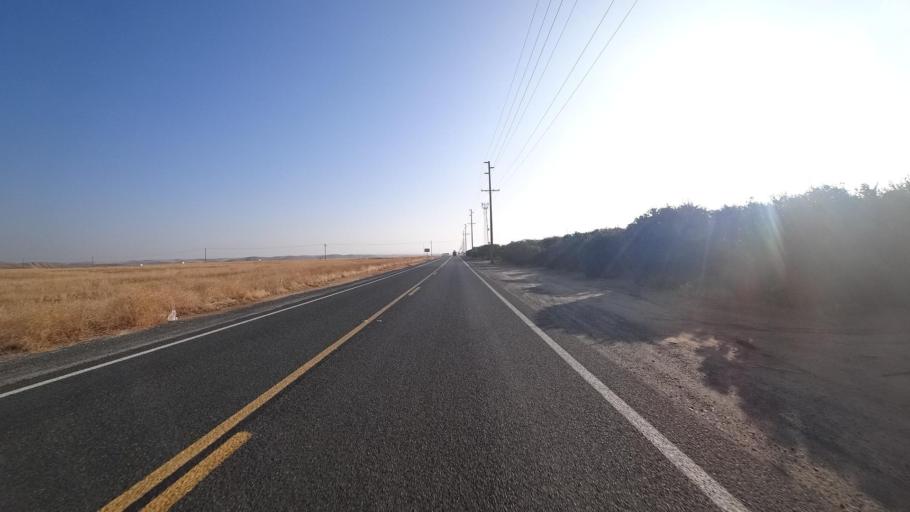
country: US
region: California
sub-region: Tulare County
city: Richgrove
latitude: 35.7620
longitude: -119.0564
